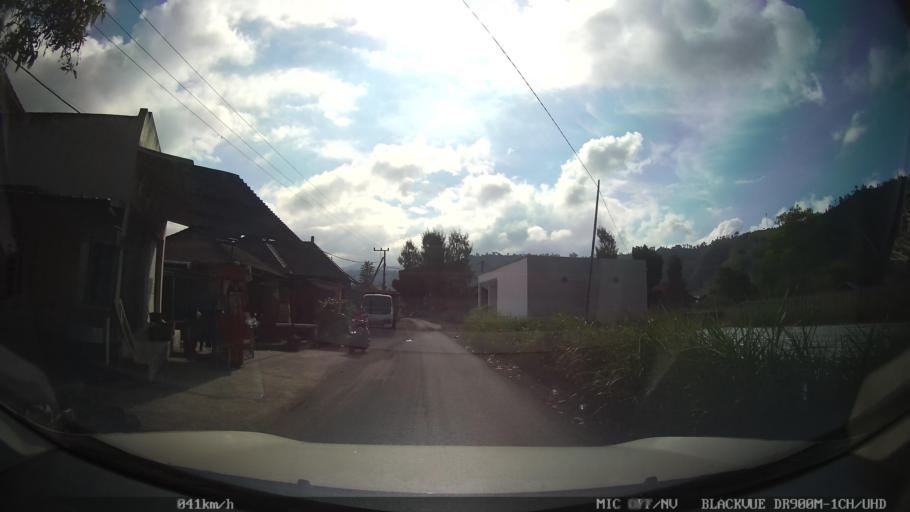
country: ID
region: Bali
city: Banjar Trunyan
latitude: -8.2167
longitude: 115.3895
